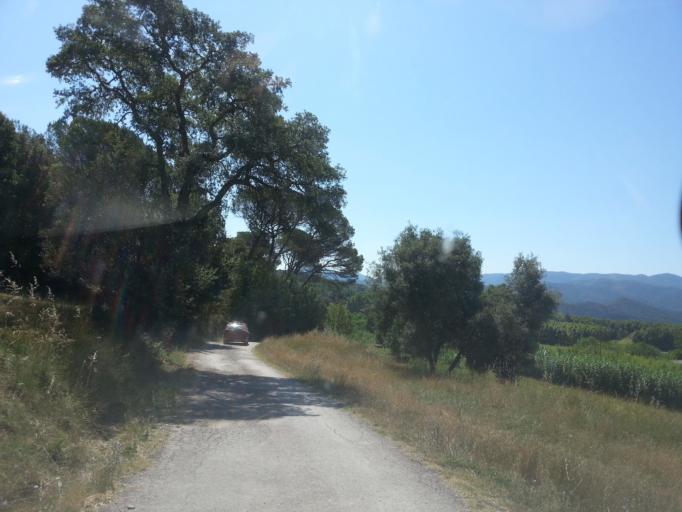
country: ES
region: Catalonia
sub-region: Provincia de Girona
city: Breda
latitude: 41.7266
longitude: 2.5168
